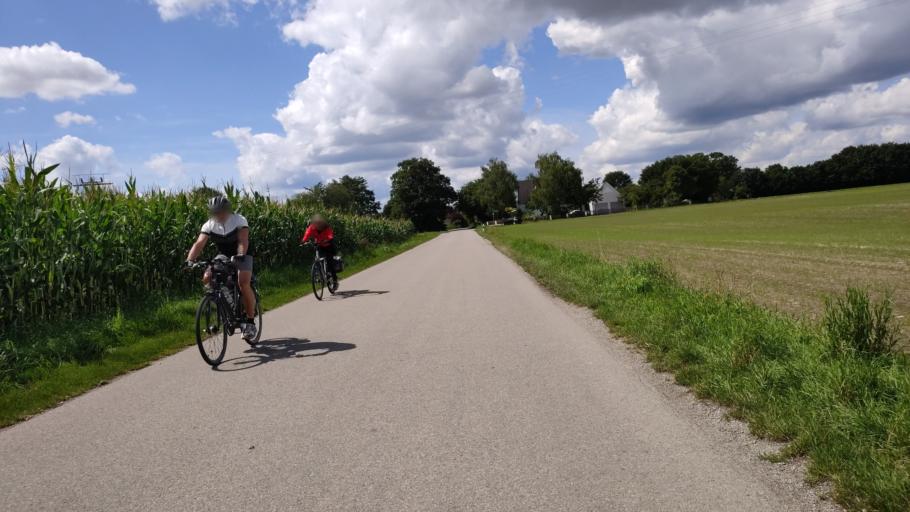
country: DE
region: Bavaria
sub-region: Swabia
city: Konigsbrunn
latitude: 48.2474
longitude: 10.9016
